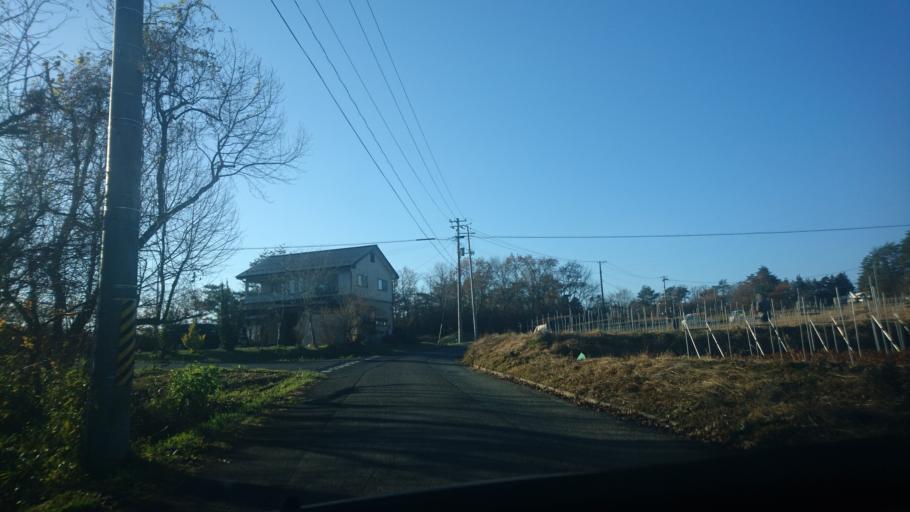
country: JP
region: Iwate
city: Ichinoseki
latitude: 38.8966
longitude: 141.2354
